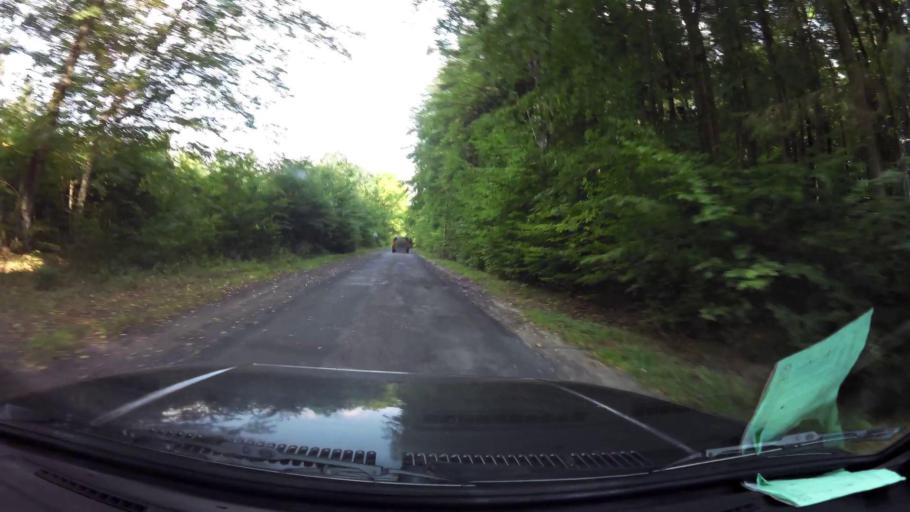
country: PL
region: West Pomeranian Voivodeship
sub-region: Powiat koszalinski
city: Bobolice
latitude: 54.1010
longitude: 16.4949
